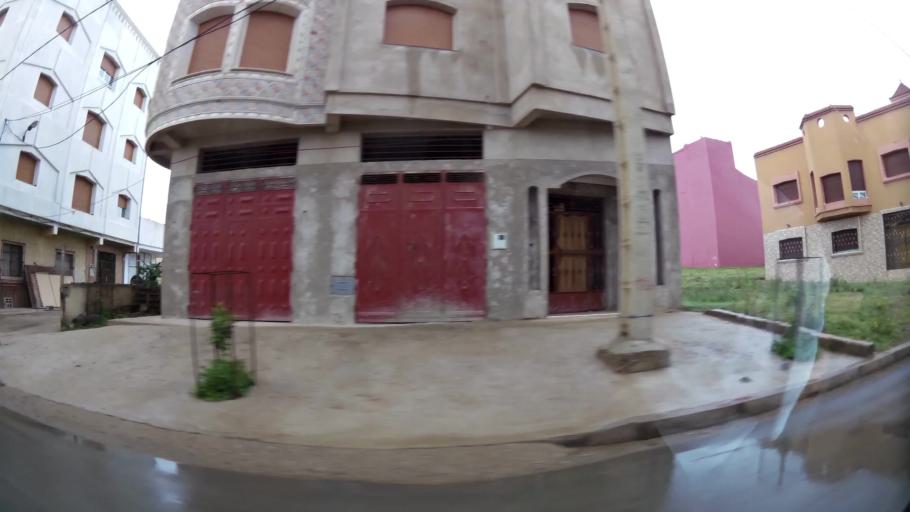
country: MA
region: Oriental
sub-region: Nador
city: Nador
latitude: 35.1503
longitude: -2.9952
